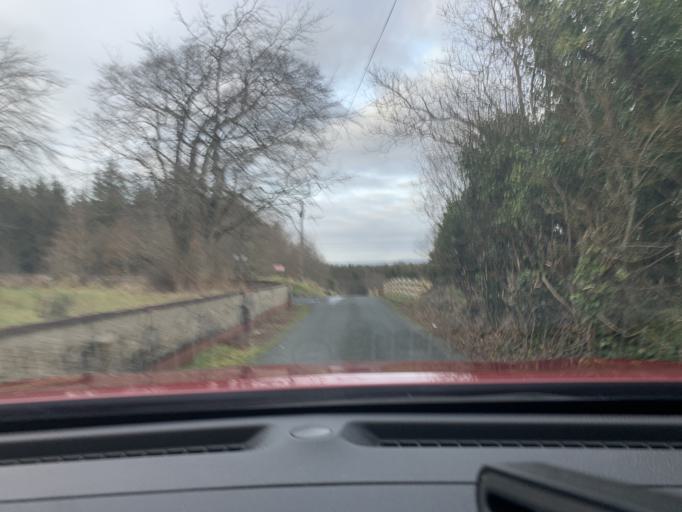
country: IE
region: Connaught
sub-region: Roscommon
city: Ballaghaderreen
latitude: 53.9765
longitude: -8.5596
